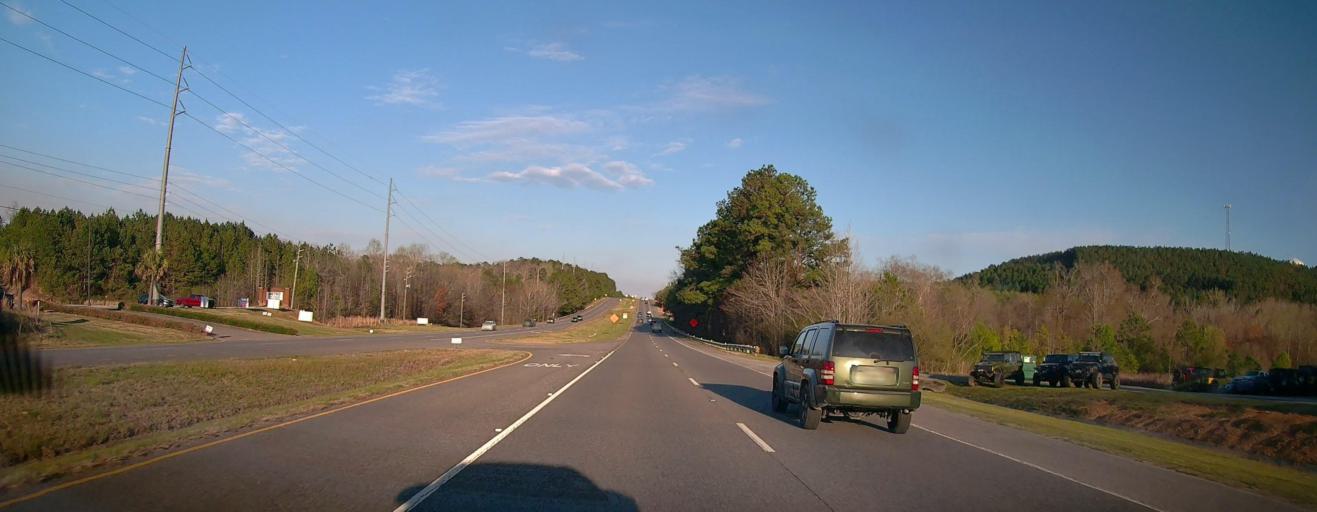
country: US
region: Alabama
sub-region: Shelby County
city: Chelsea
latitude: 33.3504
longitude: -86.5947
